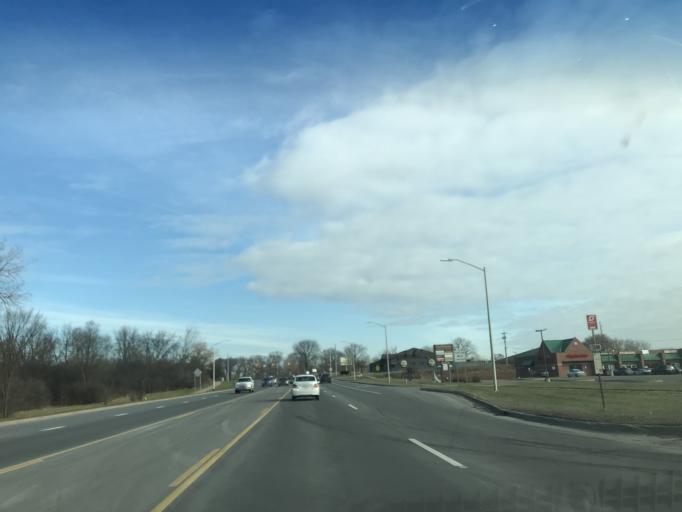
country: US
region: Michigan
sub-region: Oakland County
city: Auburn Hills
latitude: 42.6699
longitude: -83.2568
